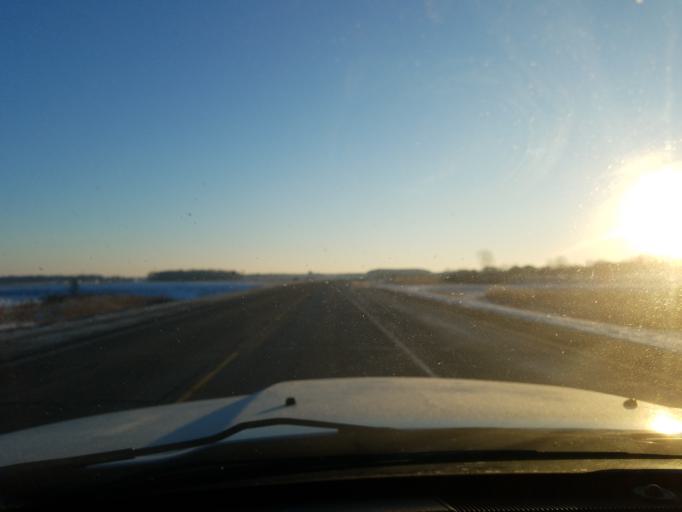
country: US
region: Indiana
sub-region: Marshall County
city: Bremen
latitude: 41.4607
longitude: -86.1480
